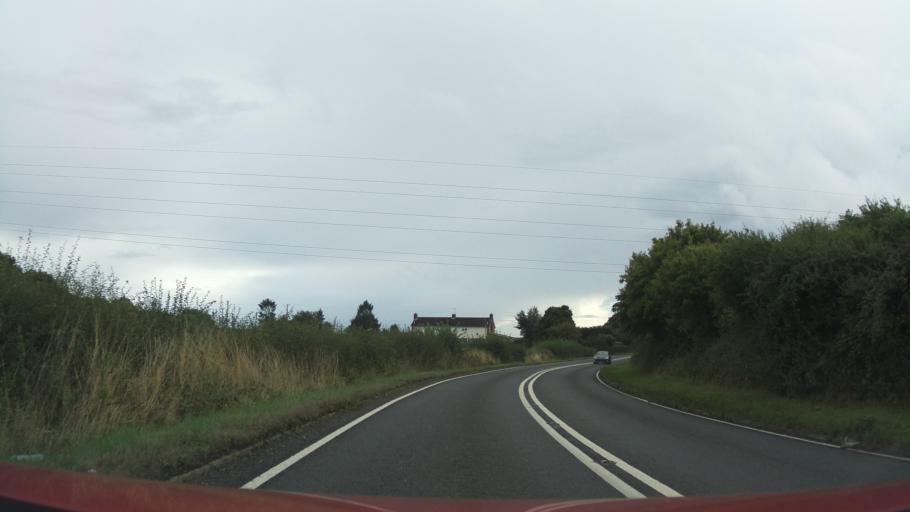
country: GB
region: England
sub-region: Worcestershire
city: Droitwich
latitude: 52.2943
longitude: -2.1711
